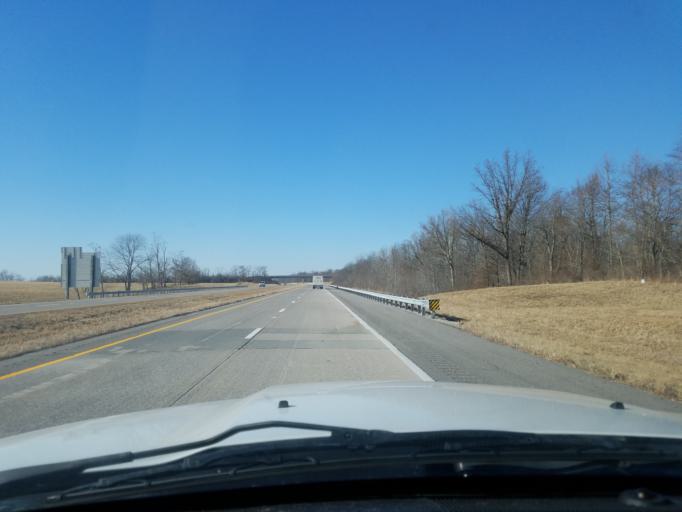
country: US
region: Indiana
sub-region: Warrick County
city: Newburgh
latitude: 37.7674
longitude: -87.4252
